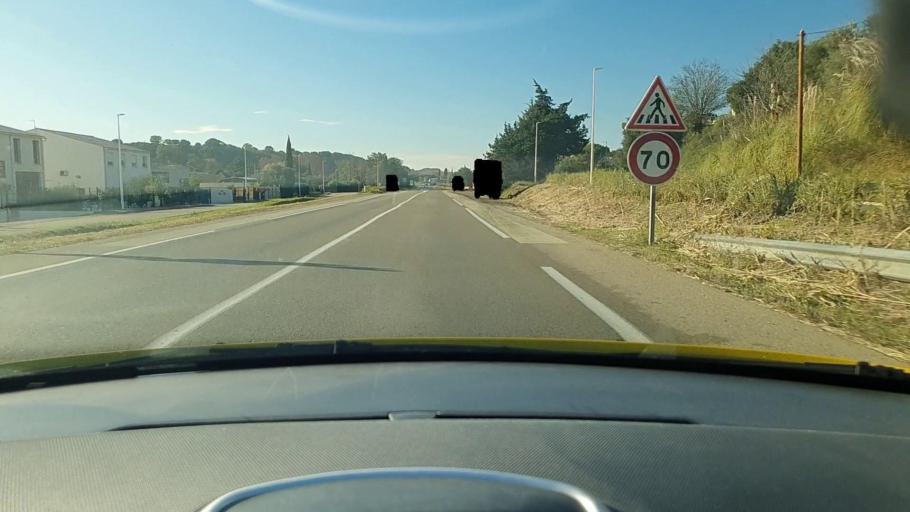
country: FR
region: Languedoc-Roussillon
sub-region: Departement du Gard
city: Bellegarde
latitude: 43.7592
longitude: 4.5137
